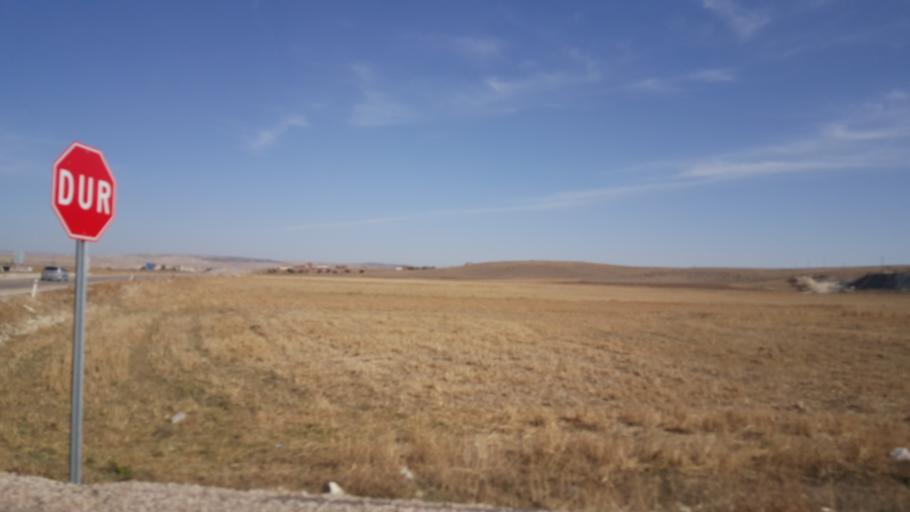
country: TR
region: Ankara
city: Yenice
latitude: 39.3826
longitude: 32.8226
